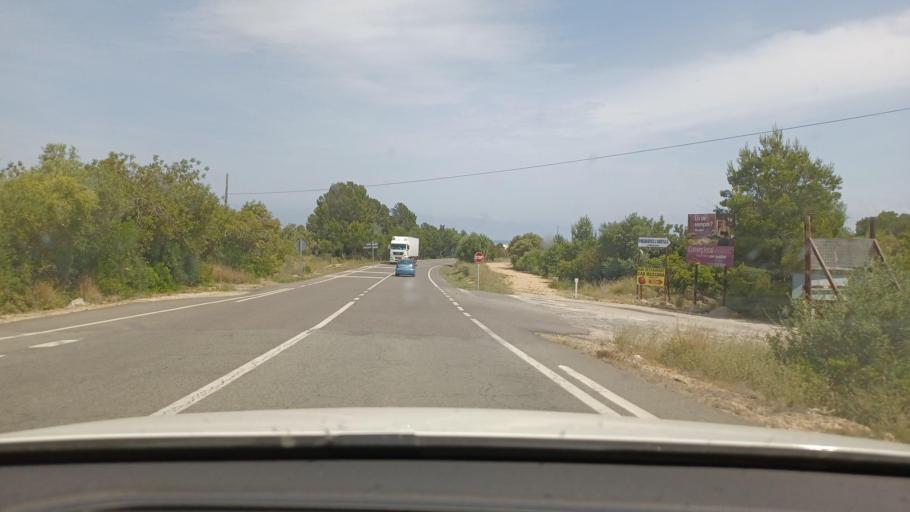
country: ES
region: Catalonia
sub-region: Provincia de Tarragona
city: l'Ametlla de Mar
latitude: 40.8940
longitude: 0.7916
